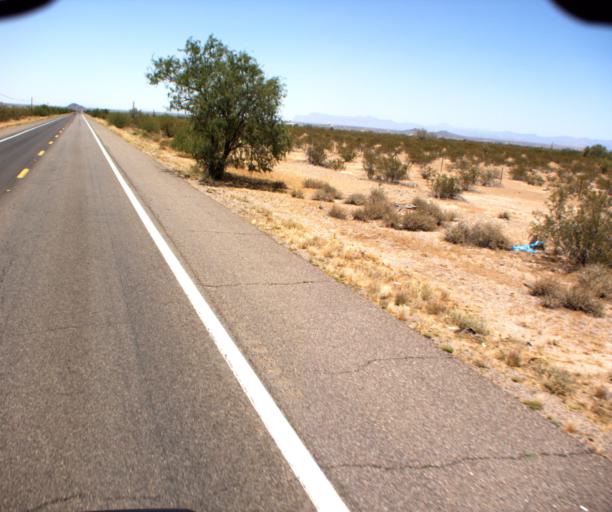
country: US
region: Arizona
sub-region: Pinal County
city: Florence
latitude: 32.9919
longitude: -111.3643
